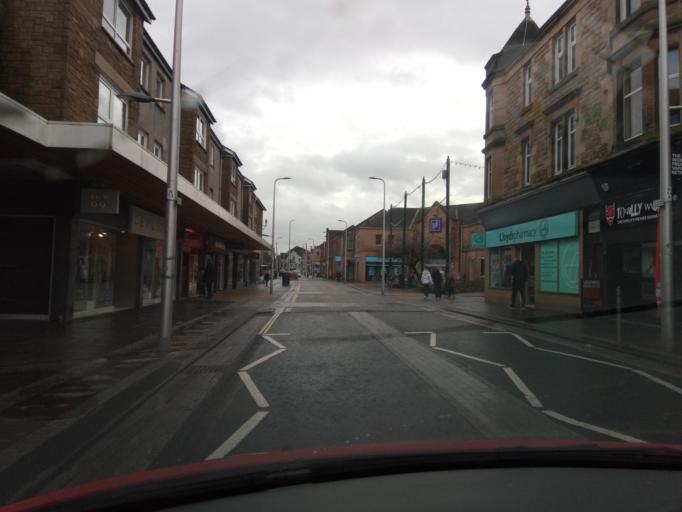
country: GB
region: Scotland
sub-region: East Dunbartonshire
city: Kirkintilloch
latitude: 55.9403
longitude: -4.1580
